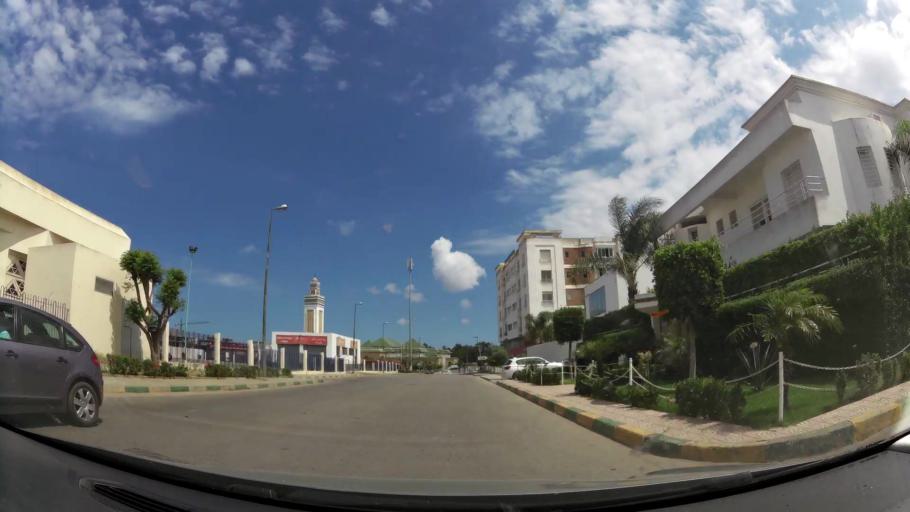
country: MA
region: Gharb-Chrarda-Beni Hssen
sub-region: Kenitra Province
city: Kenitra
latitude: 34.2477
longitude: -6.6078
